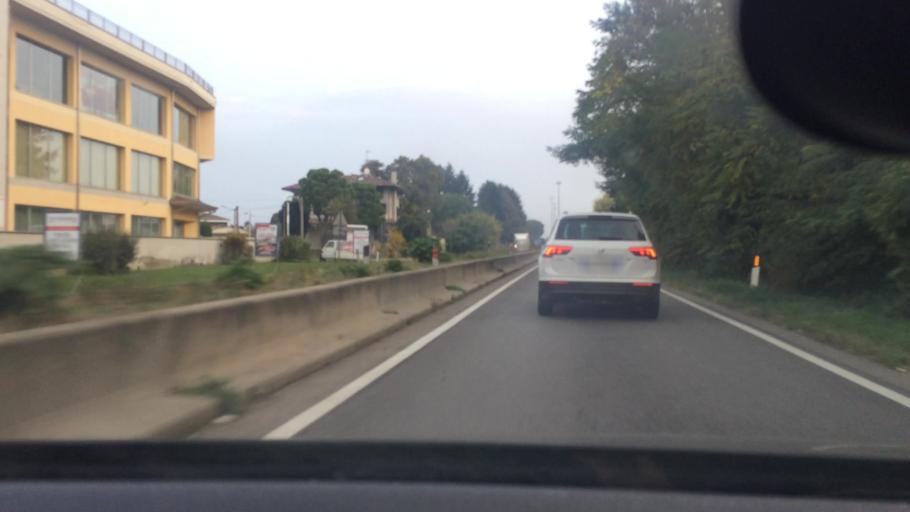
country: IT
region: Lombardy
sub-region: Citta metropolitana di Milano
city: Villa Cortese
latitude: 45.5639
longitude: 8.8960
